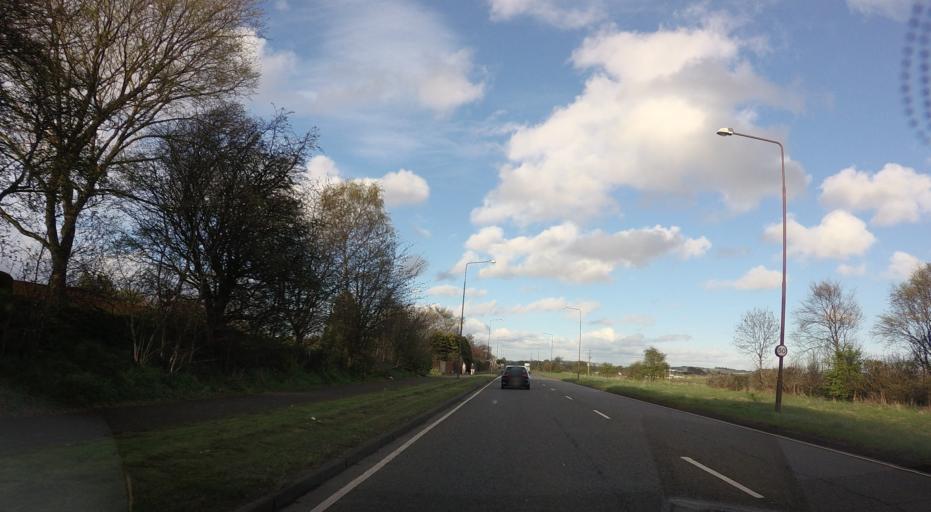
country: GB
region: Scotland
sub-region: West Lothian
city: Broxburn
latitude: 55.9314
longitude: -3.4660
